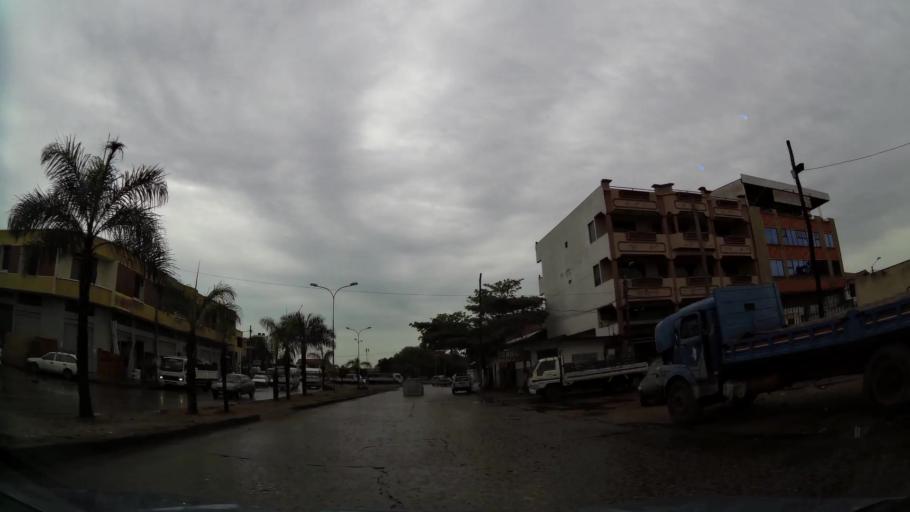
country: BO
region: Santa Cruz
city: Santa Cruz de la Sierra
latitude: -17.8116
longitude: -63.1902
